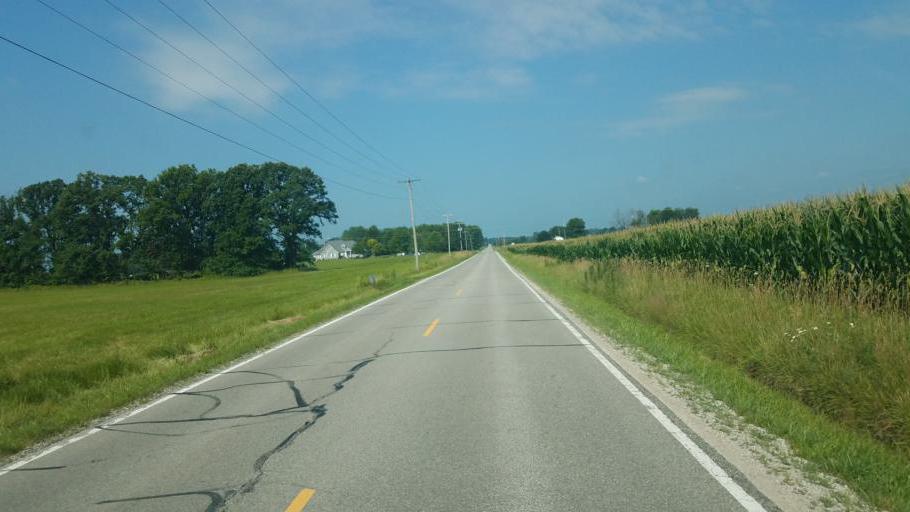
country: US
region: Ohio
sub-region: Crawford County
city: Galion
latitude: 40.7562
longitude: -82.8162
